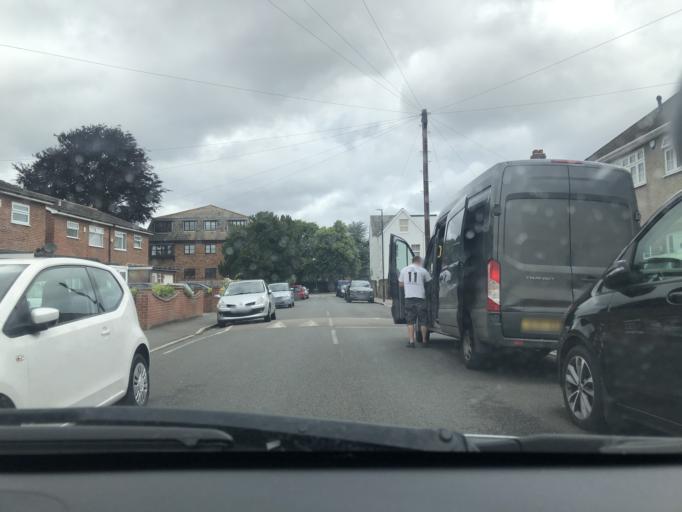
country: GB
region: England
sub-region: Greater London
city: Bexleyheath
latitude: 51.4584
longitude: 0.1275
